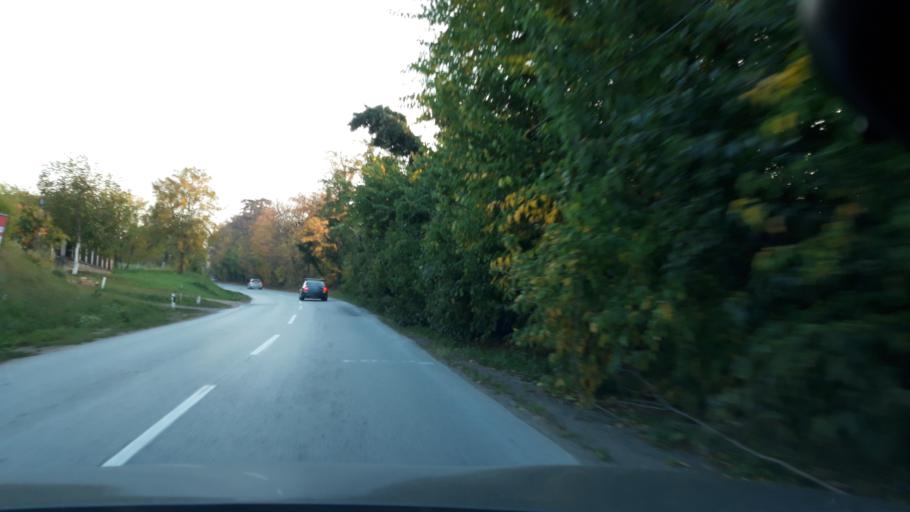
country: RS
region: Autonomna Pokrajina Vojvodina
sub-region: Juznobacki Okrug
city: Novi Sad
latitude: 45.2083
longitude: 19.8408
